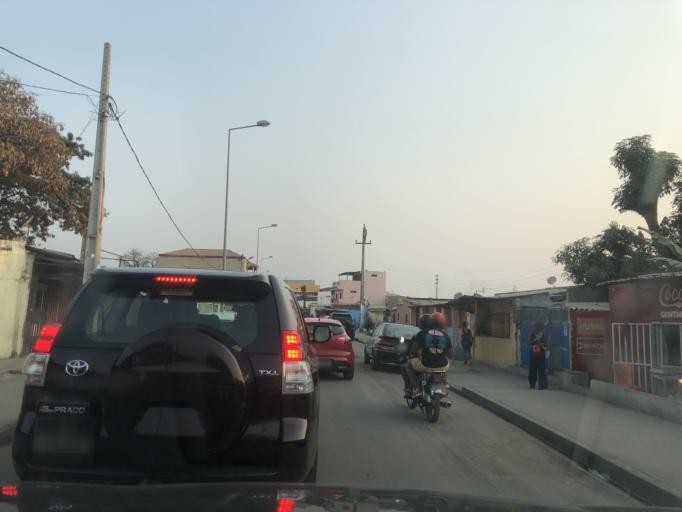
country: AO
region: Luanda
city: Luanda
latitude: -8.8429
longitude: 13.2251
